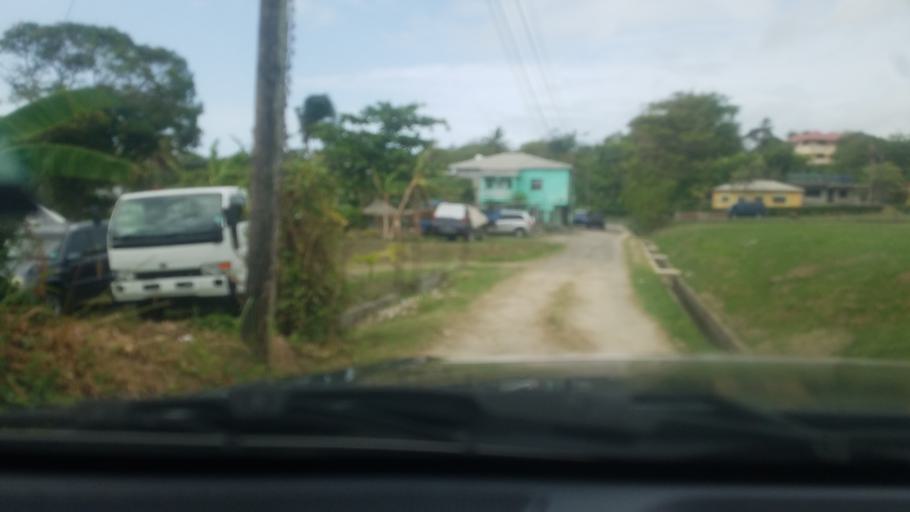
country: LC
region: Micoud Quarter
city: Micoud
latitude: 13.7981
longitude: -60.9148
